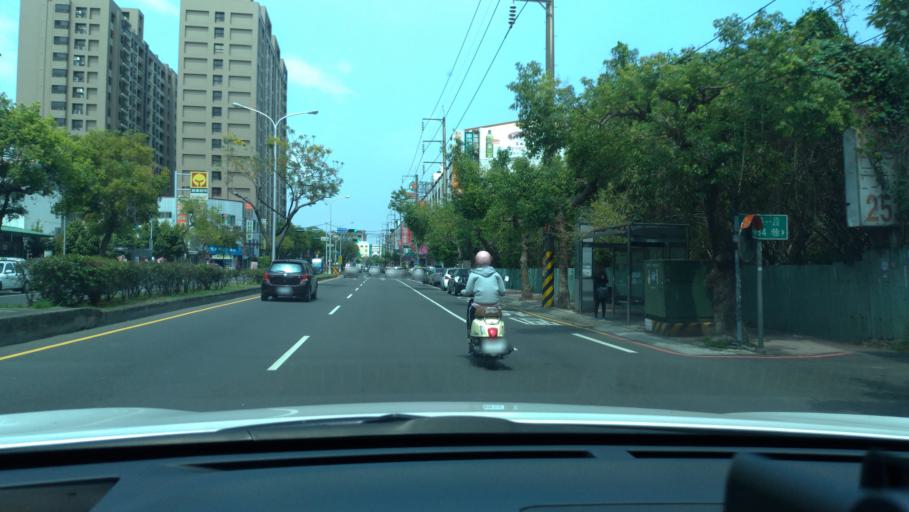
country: TW
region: Taiwan
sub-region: Taichung City
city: Taichung
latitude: 24.1912
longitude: 120.7026
